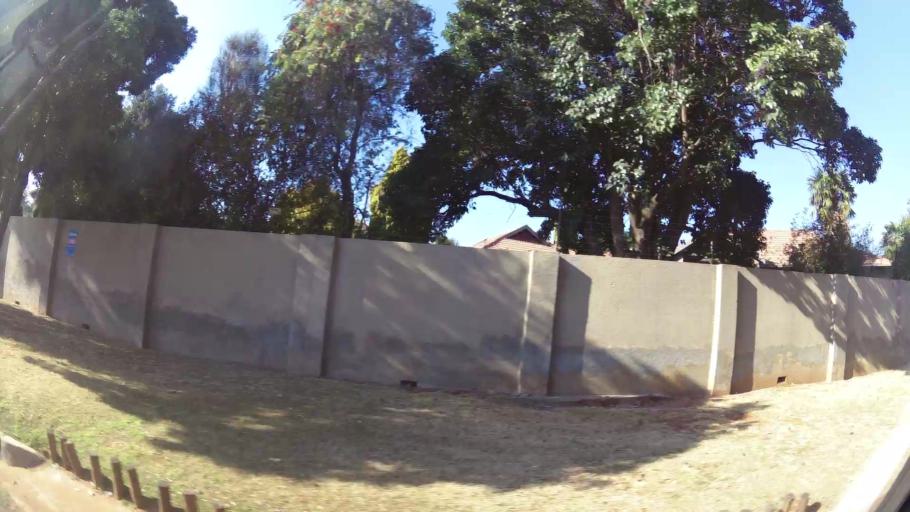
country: ZA
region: Gauteng
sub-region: Ekurhuleni Metropolitan Municipality
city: Germiston
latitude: -26.1757
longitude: 28.1503
